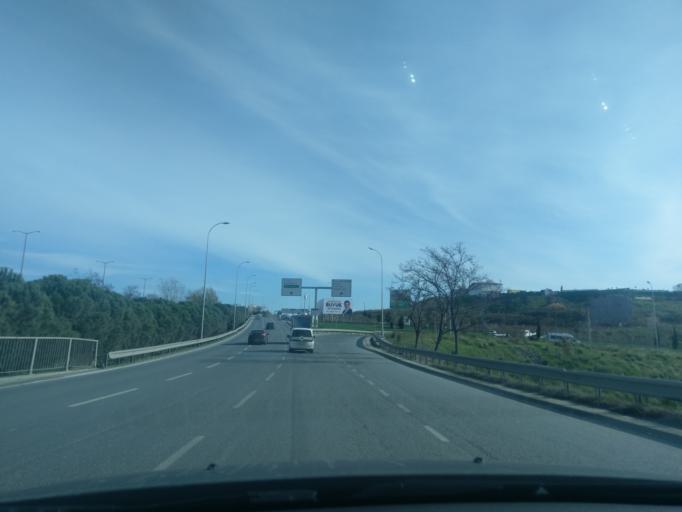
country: TR
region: Istanbul
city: Basaksehir
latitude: 41.0606
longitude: 28.7570
